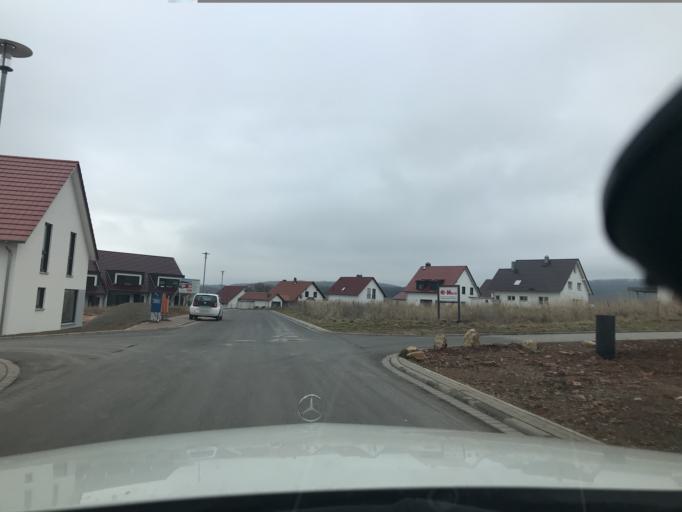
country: DE
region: Thuringia
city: Kallmerode
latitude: 51.3753
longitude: 10.2785
